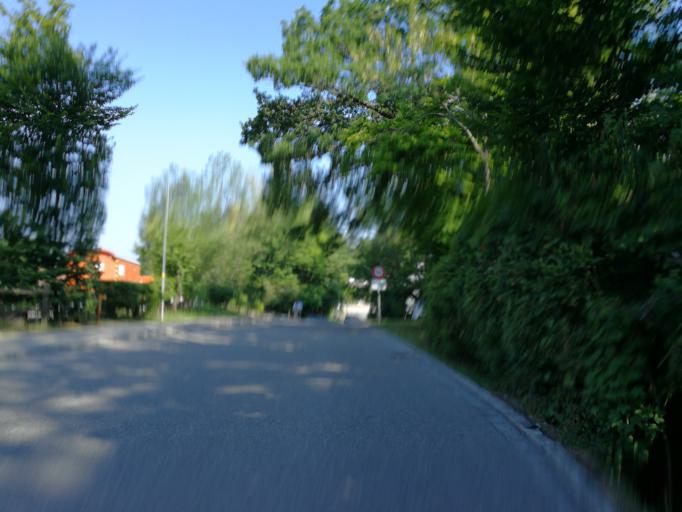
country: CH
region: Zurich
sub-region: Bezirk Meilen
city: Erlenbach / links des Dorfbachs oberhalb Bahnlinie
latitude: 47.3011
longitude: 8.6117
